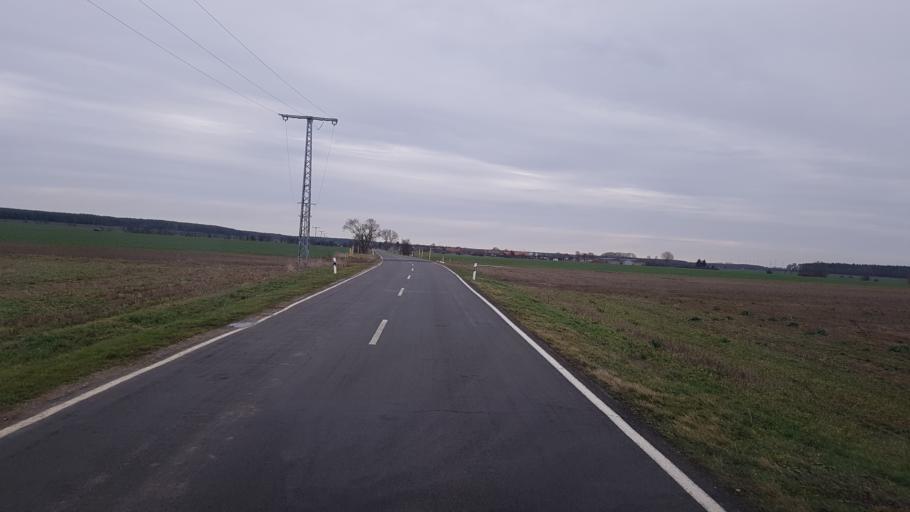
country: DE
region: Brandenburg
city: Sonnewalde
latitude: 51.7094
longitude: 13.6790
